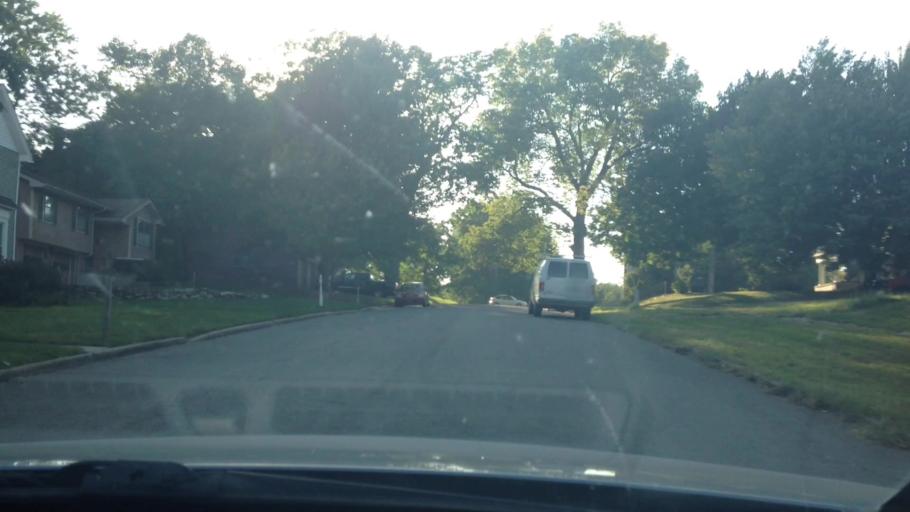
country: US
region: Kansas
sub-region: Leavenworth County
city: Leavenworth
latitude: 39.3145
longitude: -94.9195
